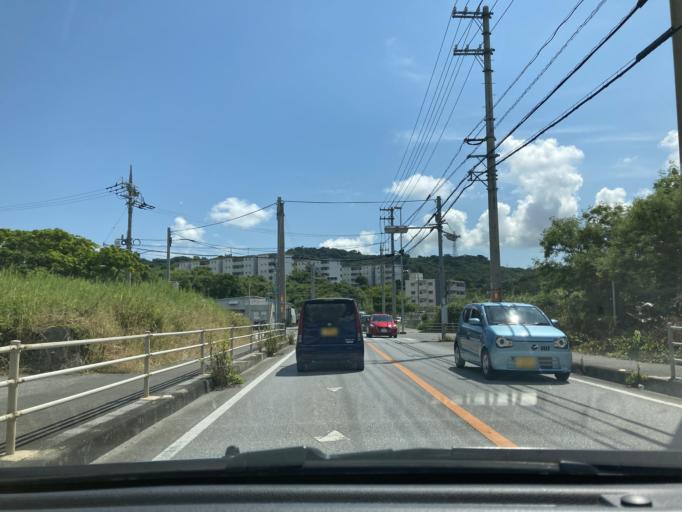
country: JP
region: Okinawa
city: Tomigusuku
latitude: 26.1756
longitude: 127.7495
